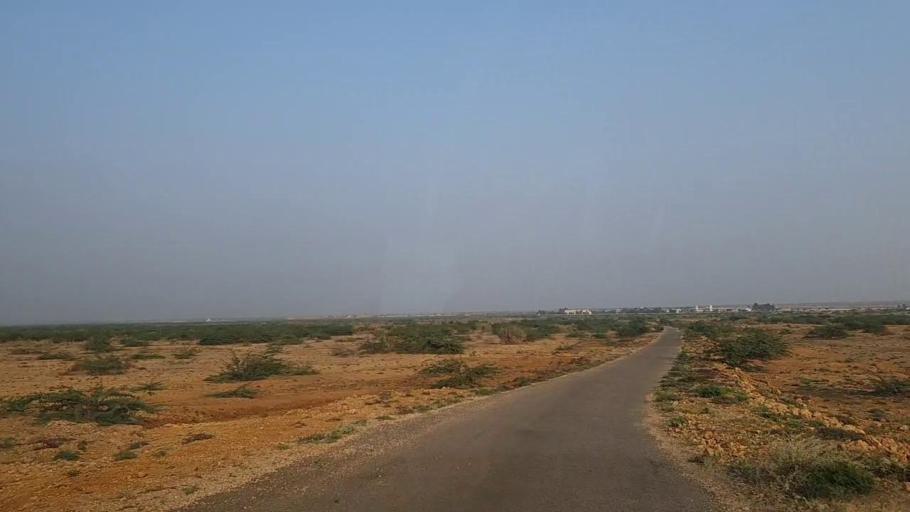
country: PK
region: Sindh
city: Thatta
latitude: 24.6908
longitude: 67.8347
